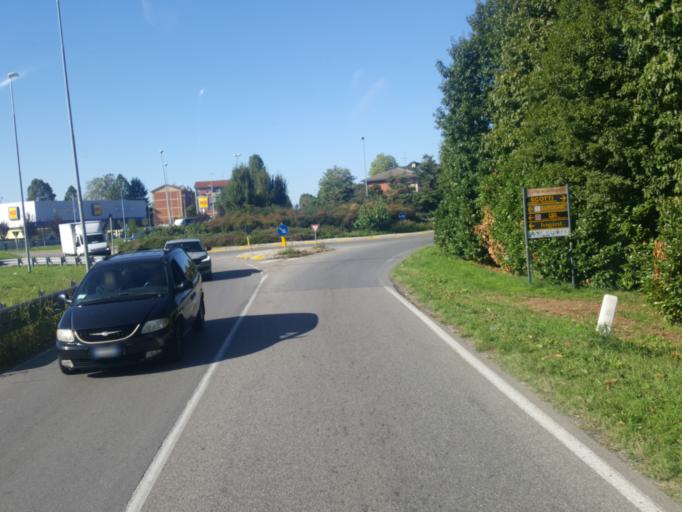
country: IT
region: Lombardy
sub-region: Citta metropolitana di Milano
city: Vittuone
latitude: 45.4837
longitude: 8.9466
